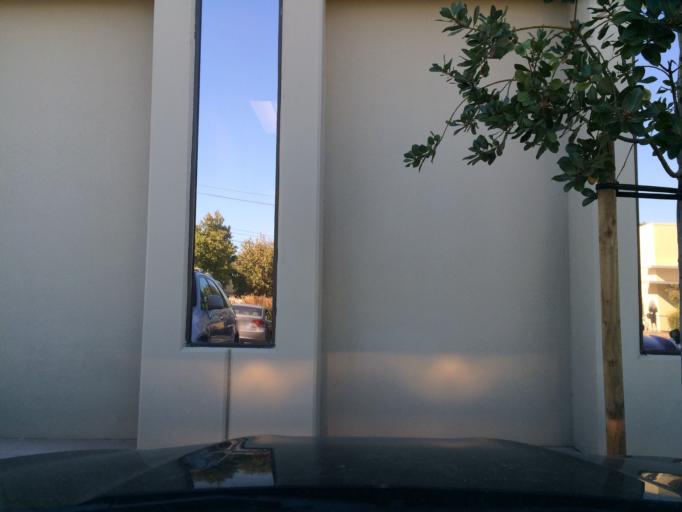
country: US
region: California
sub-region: Santa Clara County
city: Sunnyvale
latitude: 37.4026
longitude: -122.0506
